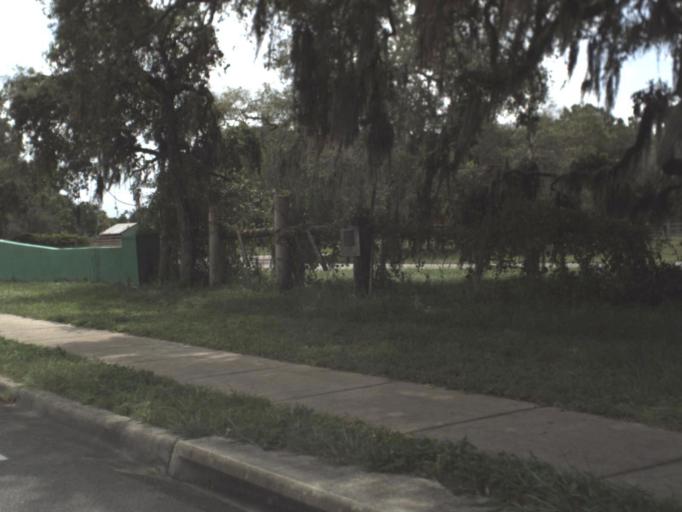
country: US
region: Florida
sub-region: Pasco County
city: Shady Hills
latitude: 28.3303
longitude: -82.5643
